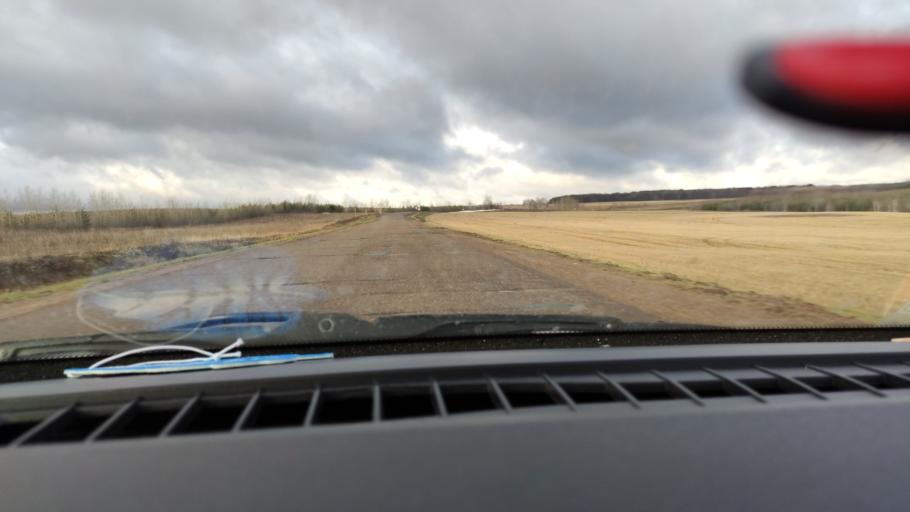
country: RU
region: Tatarstan
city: Russkiy Aktash
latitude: 55.0342
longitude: 52.0173
